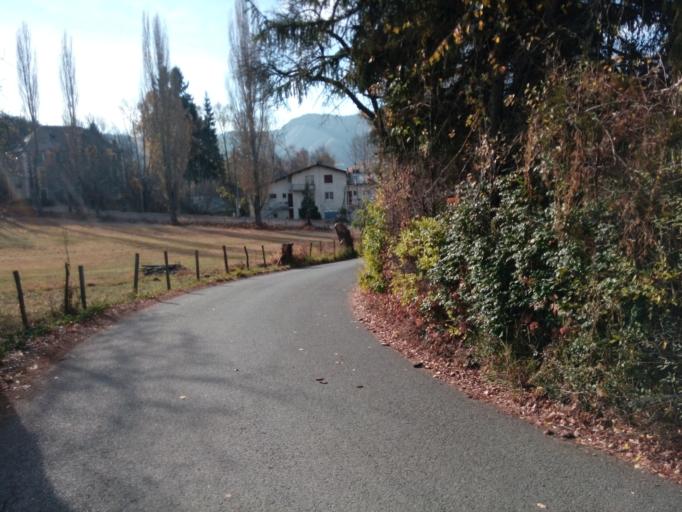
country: FR
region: Provence-Alpes-Cote d'Azur
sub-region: Departement des Alpes-de-Haute-Provence
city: Seyne-les-Alpes
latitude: 44.3487
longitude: 6.3563
